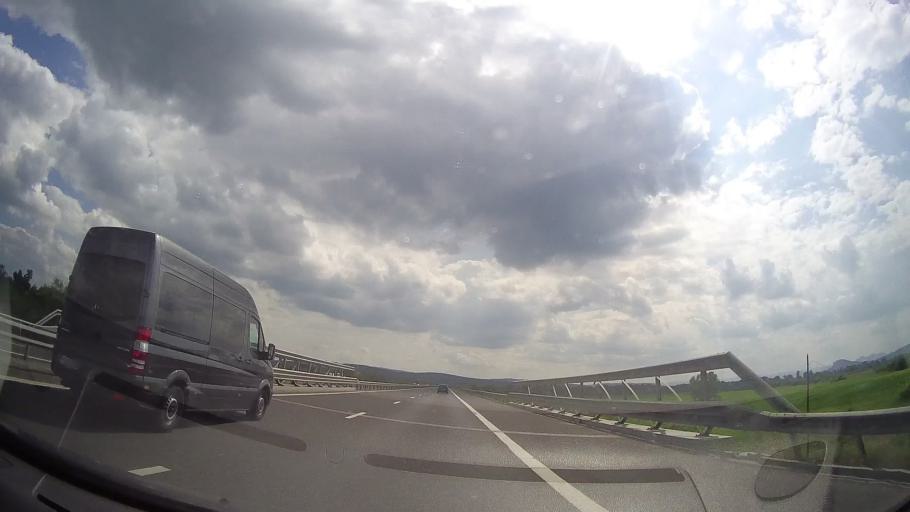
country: RO
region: Hunedoara
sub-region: Comuna Turdas
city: Pricaz
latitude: 45.8605
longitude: 23.1481
